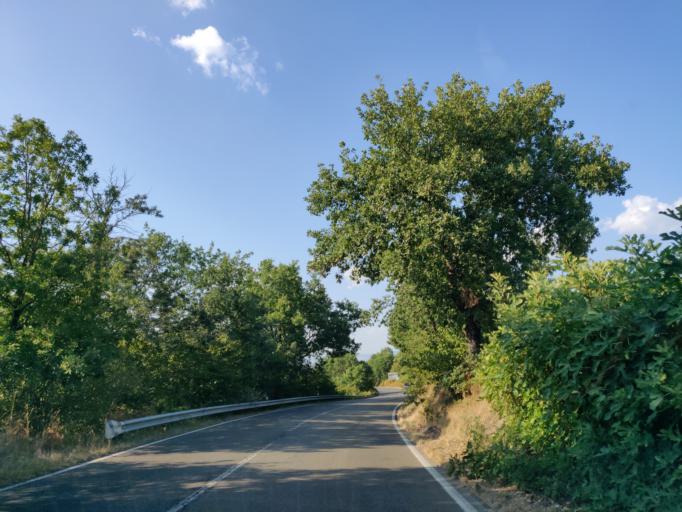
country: IT
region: Latium
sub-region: Provincia di Viterbo
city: Latera
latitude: 42.6360
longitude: 11.8363
